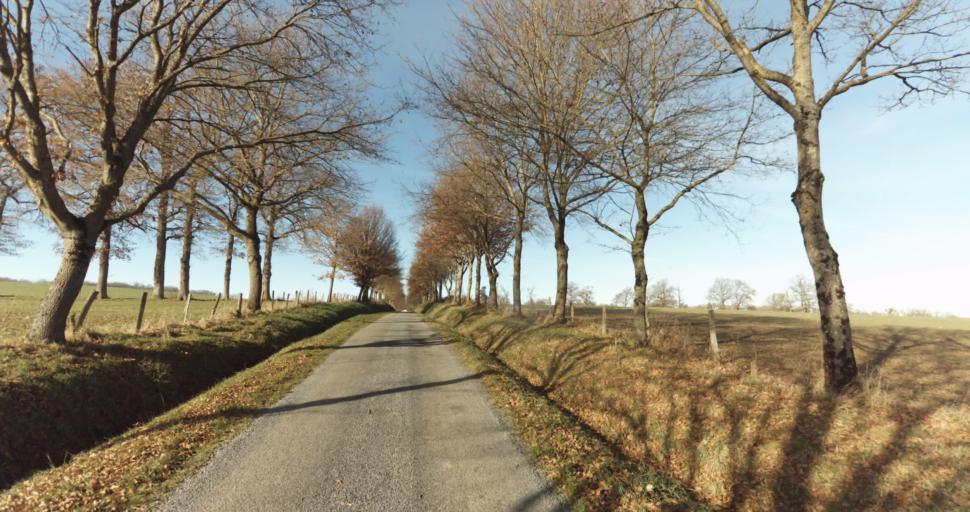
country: FR
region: Limousin
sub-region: Departement de la Haute-Vienne
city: Saint-Priest-sous-Aixe
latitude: 45.7856
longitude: 1.1079
